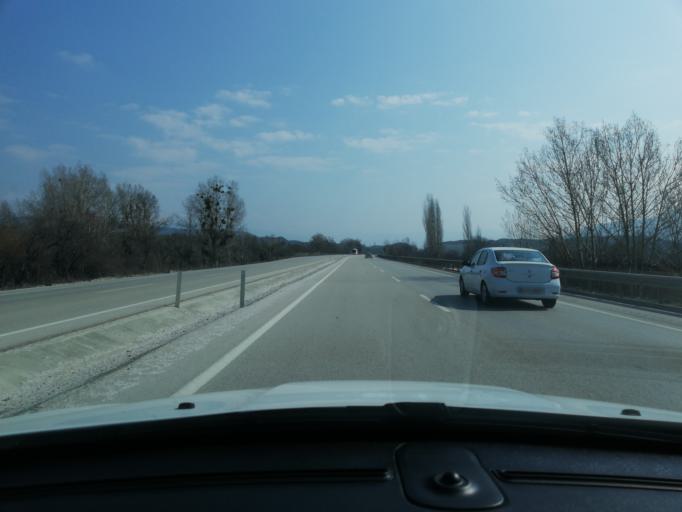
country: TR
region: Cankiri
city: Beloren
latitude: 40.8725
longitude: 33.4978
